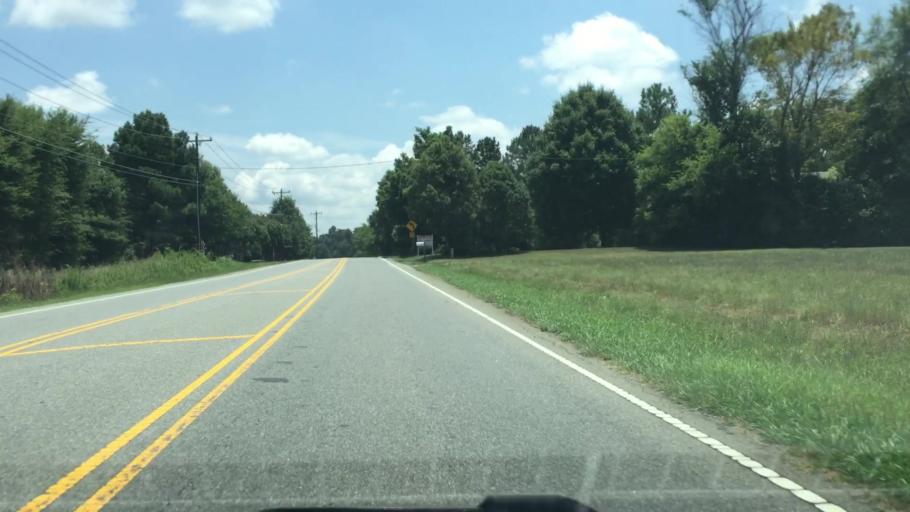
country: US
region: North Carolina
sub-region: Rowan County
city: Enochville
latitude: 35.4330
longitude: -80.7246
